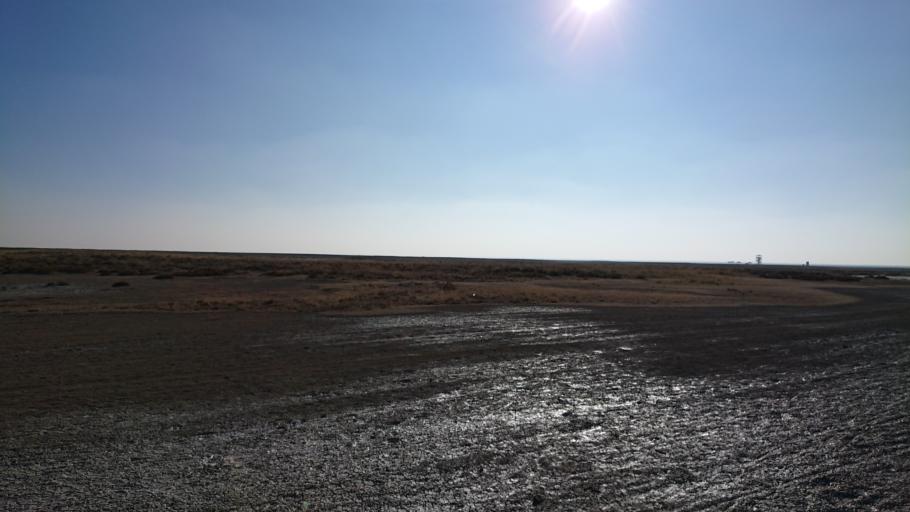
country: TR
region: Aksaray
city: Eskil
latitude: 38.4300
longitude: 33.5067
